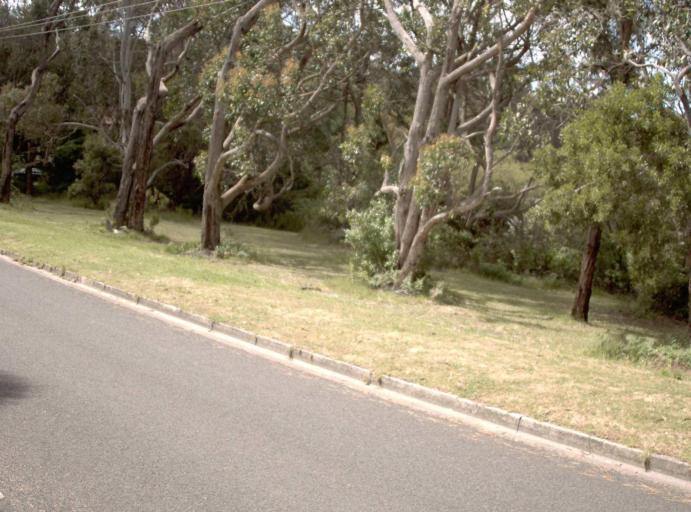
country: AU
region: Victoria
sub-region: Mornington Peninsula
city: Dromana
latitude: -38.3550
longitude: 144.9567
